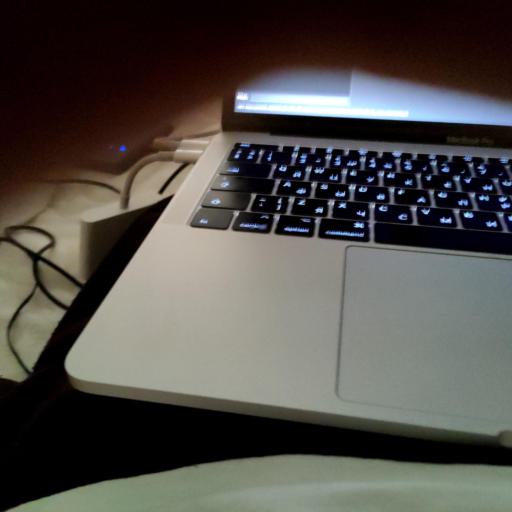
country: RU
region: Volgograd
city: Gorodishche
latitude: 48.8551
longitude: 44.4863
